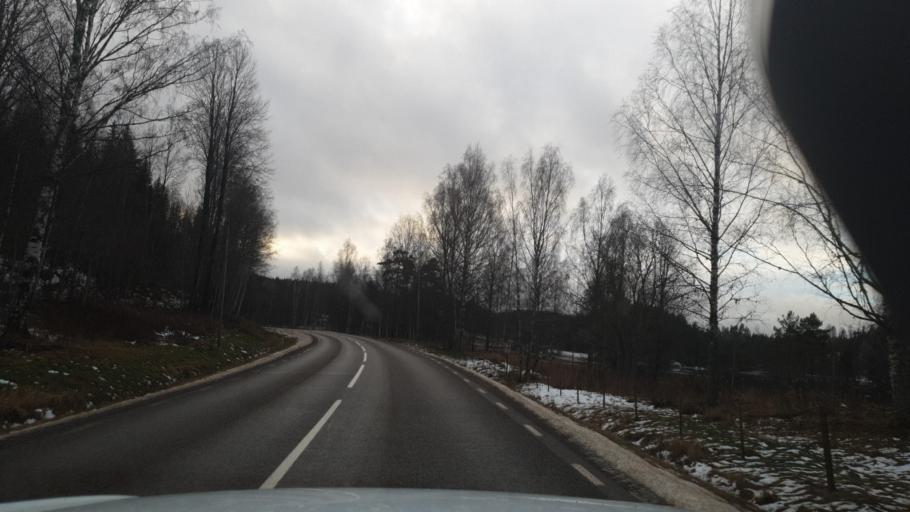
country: SE
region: Vaermland
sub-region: Eda Kommun
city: Amotfors
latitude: 59.6969
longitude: 12.4289
